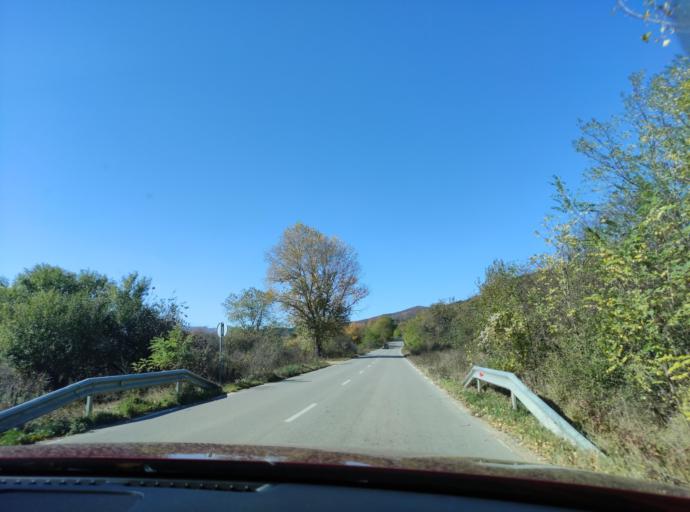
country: BG
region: Montana
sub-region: Obshtina Chiprovtsi
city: Chiprovtsi
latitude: 43.4301
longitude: 22.9945
